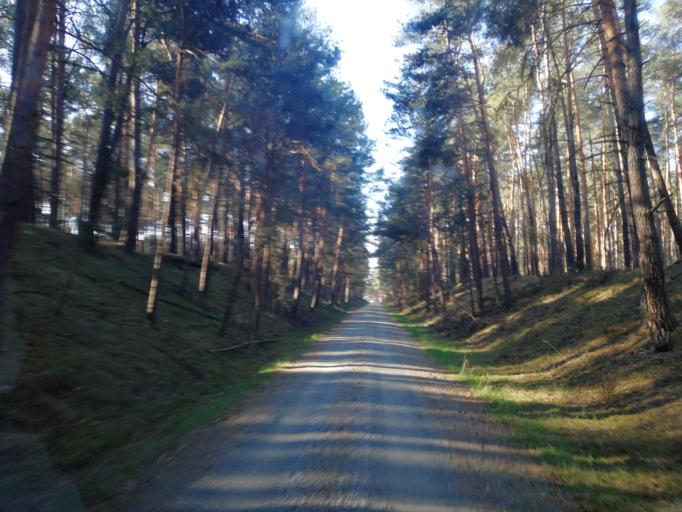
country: DE
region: Brandenburg
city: Drahnsdorf
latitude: 51.8917
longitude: 13.5270
